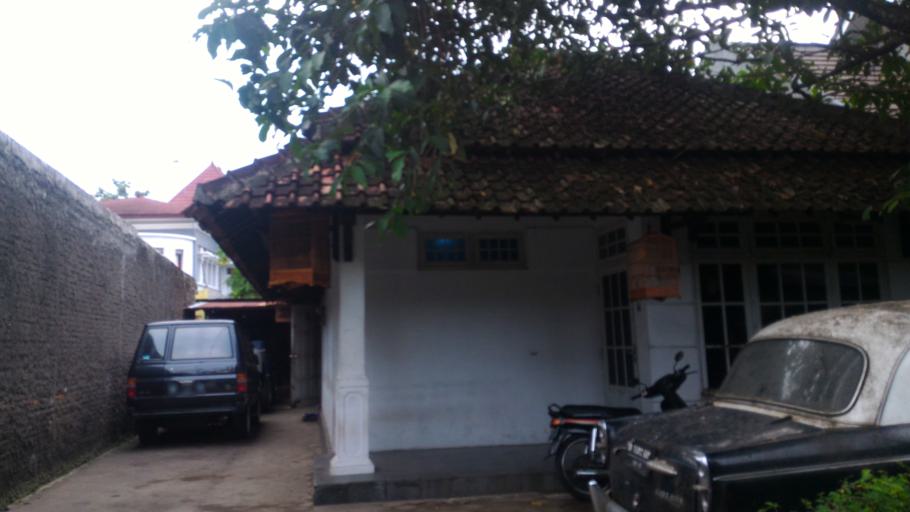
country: ID
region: Daerah Istimewa Yogyakarta
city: Kasihan
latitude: -7.8183
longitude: 110.3570
